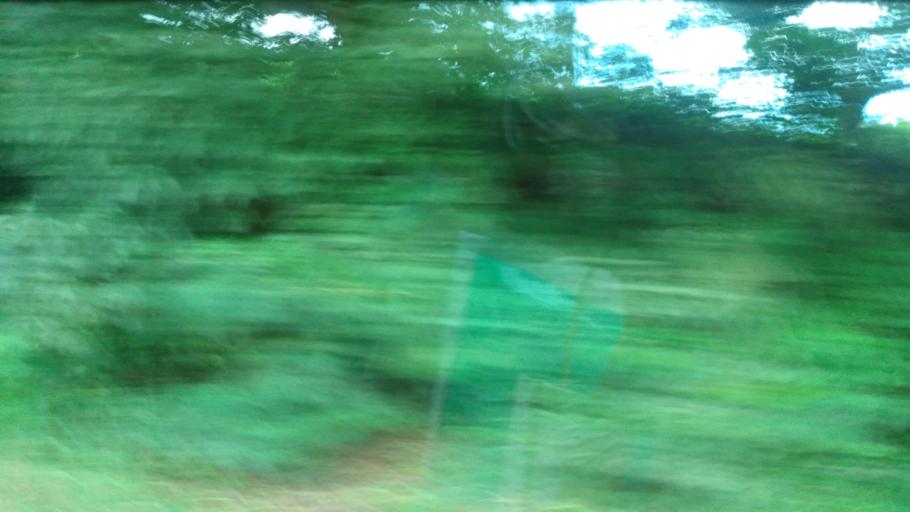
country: BR
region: Pernambuco
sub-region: Maraial
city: Maraial
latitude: -8.7199
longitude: -35.7815
